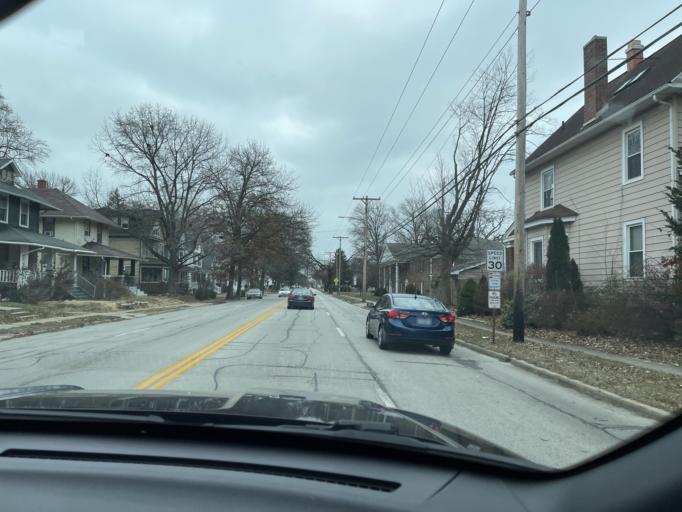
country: US
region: Illinois
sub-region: Sangamon County
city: Leland Grove
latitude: 39.7941
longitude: -89.6743
